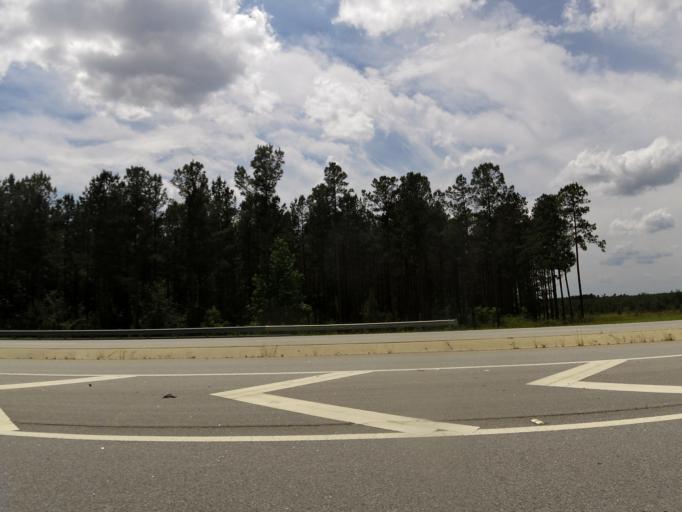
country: US
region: Georgia
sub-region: Emanuel County
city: Swainsboro
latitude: 32.7155
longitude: -82.3919
